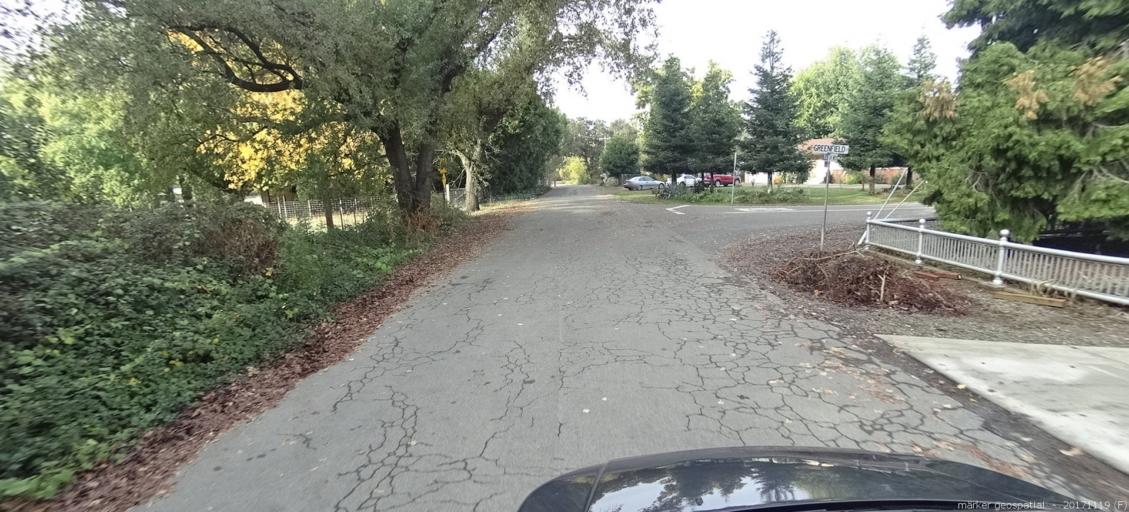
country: US
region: California
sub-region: Shasta County
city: Redding
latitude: 40.5148
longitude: -122.3488
